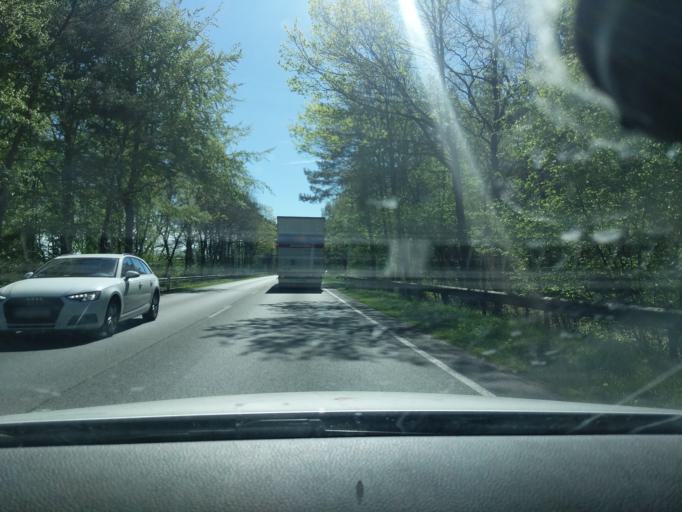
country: DE
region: Lower Saxony
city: Buxtehude
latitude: 53.4582
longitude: 9.7218
